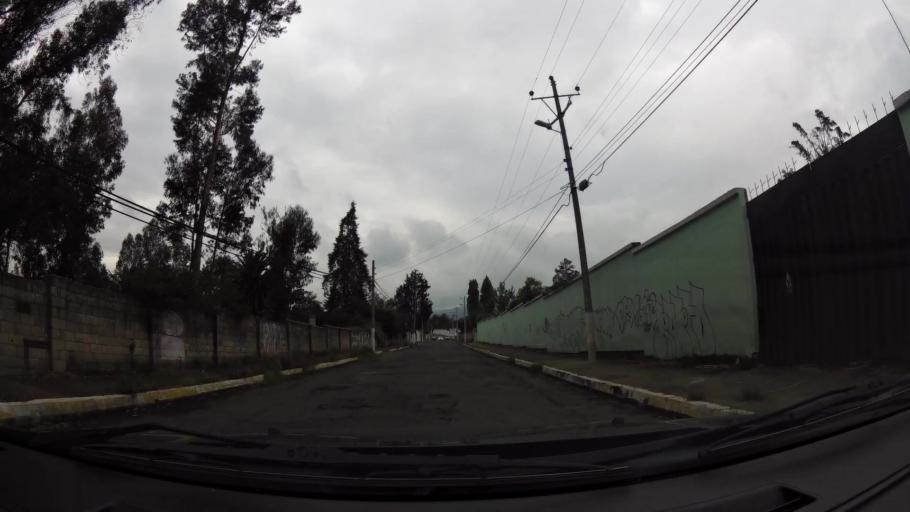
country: EC
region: Pichincha
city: Sangolqui
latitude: -0.3020
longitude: -78.4699
